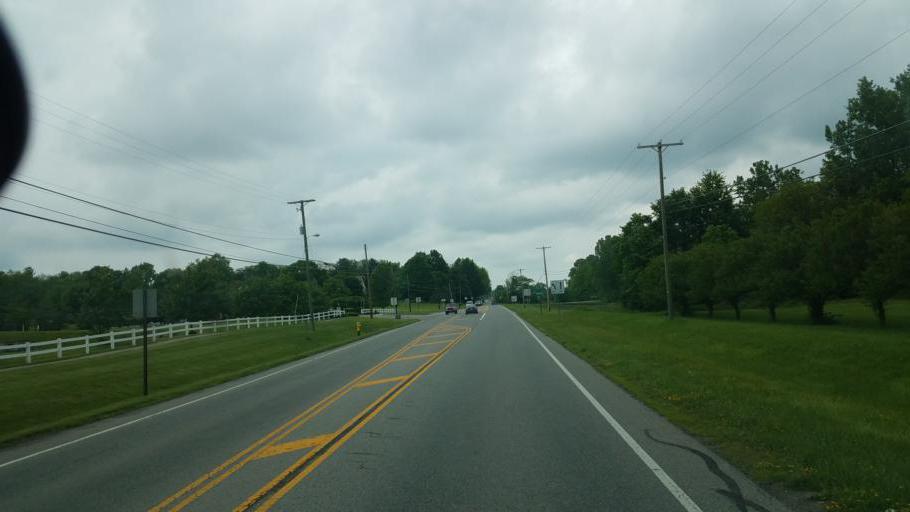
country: US
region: Ohio
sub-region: Delaware County
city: Delaware
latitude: 40.3139
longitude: -83.1157
